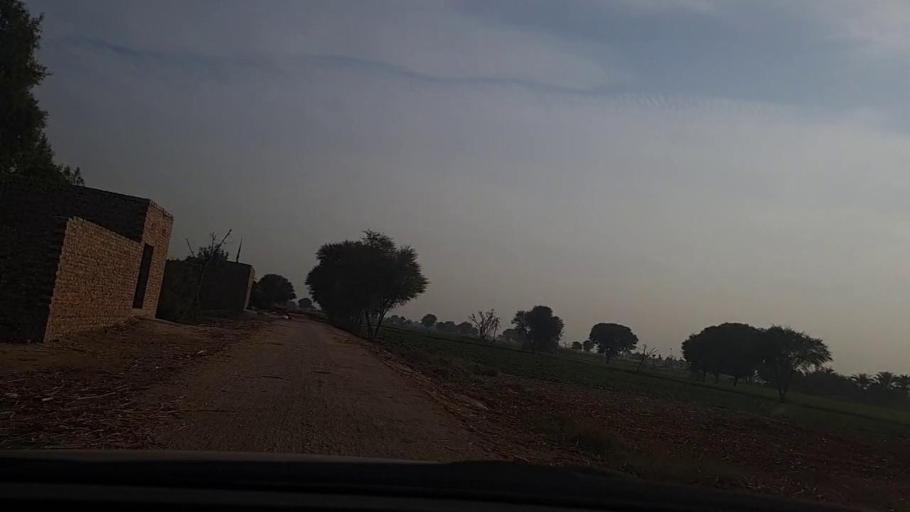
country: PK
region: Sindh
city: Daulatpur
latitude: 26.3319
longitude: 68.0549
